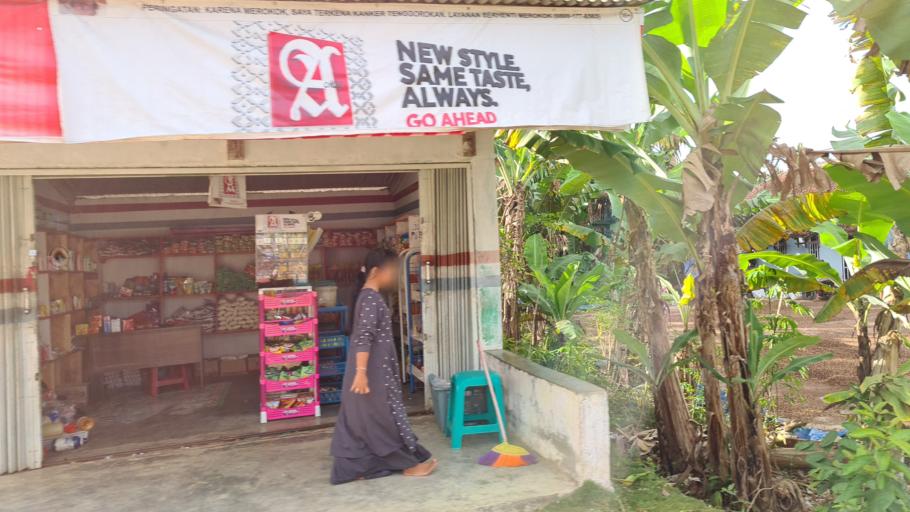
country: ID
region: Lampung
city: Kenali
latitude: -5.0926
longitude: 104.4006
